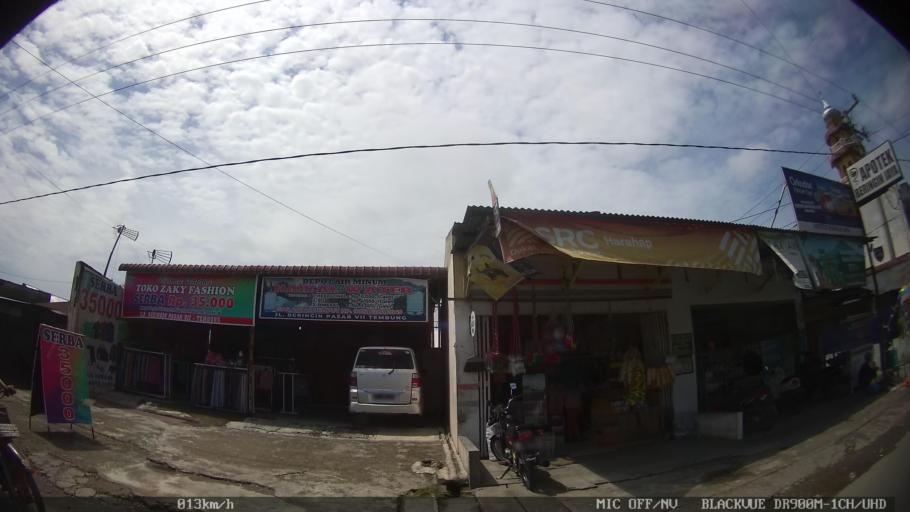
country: ID
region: North Sumatra
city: Medan
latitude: 3.5909
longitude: 98.7470
